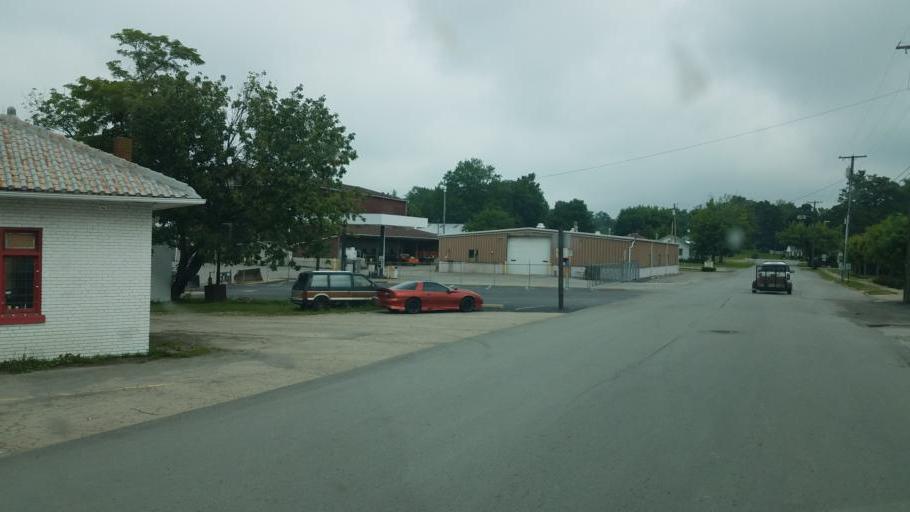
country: US
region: Ohio
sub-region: Highland County
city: Hillsboro
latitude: 39.2002
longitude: -83.5985
